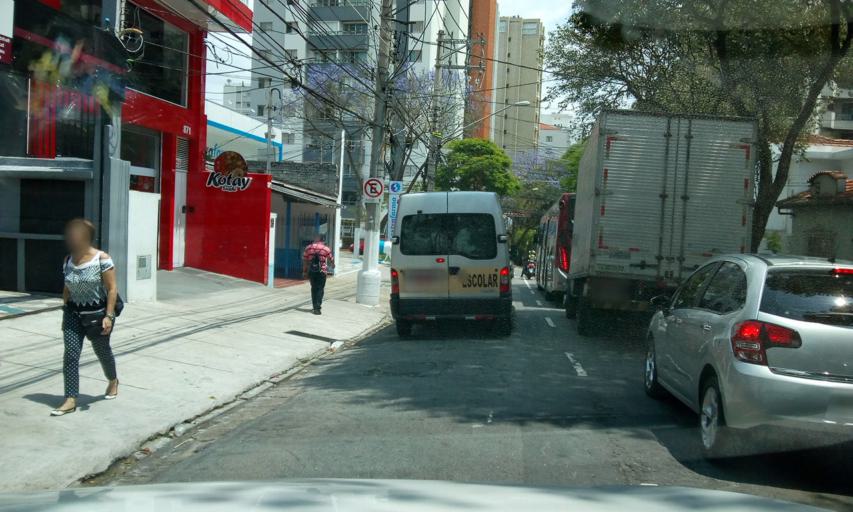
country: BR
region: Sao Paulo
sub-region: Sao Paulo
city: Sao Paulo
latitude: -23.5860
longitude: -46.6408
